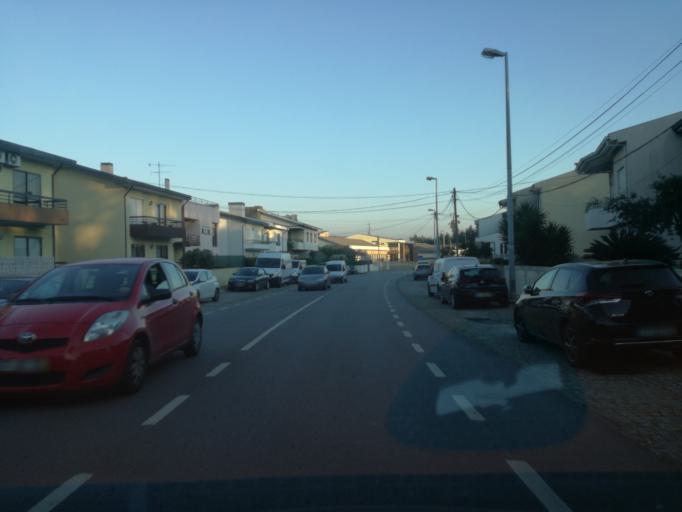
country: PT
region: Porto
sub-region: Maia
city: Leca do Bailio
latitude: 41.2231
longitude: -8.6013
